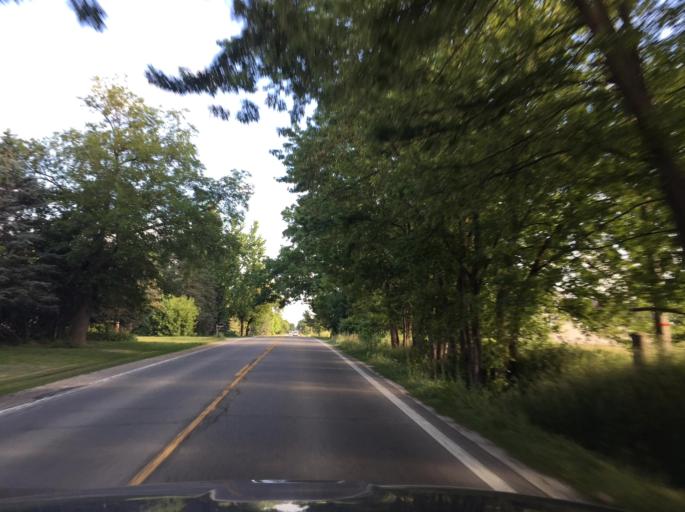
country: US
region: Michigan
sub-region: Macomb County
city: Romeo
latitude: 42.7801
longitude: -82.9617
